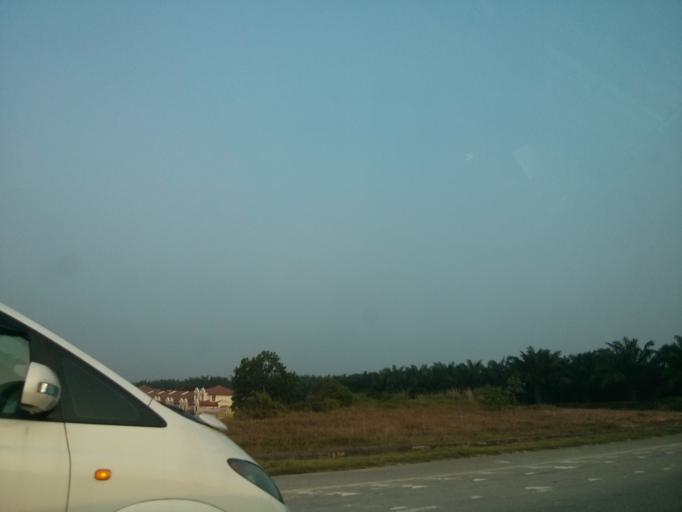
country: MY
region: Negeri Sembilan
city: Kampung Baharu Nilai
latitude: 2.8276
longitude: 101.6932
